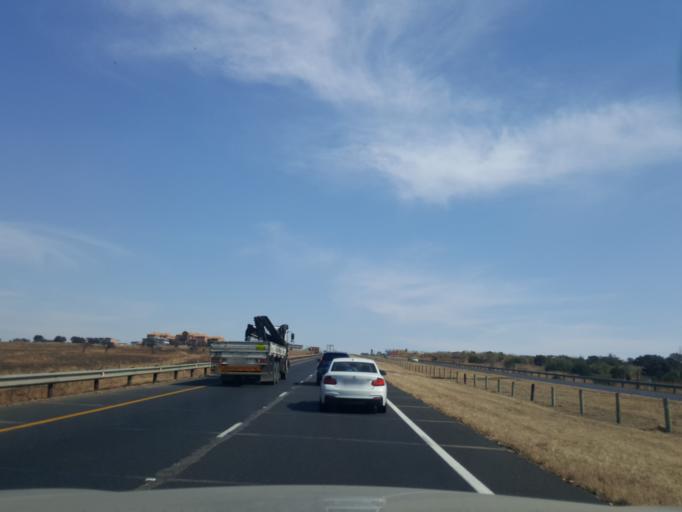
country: ZA
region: Mpumalanga
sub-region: Nkangala District Municipality
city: Witbank
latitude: -25.8811
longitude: 29.2834
